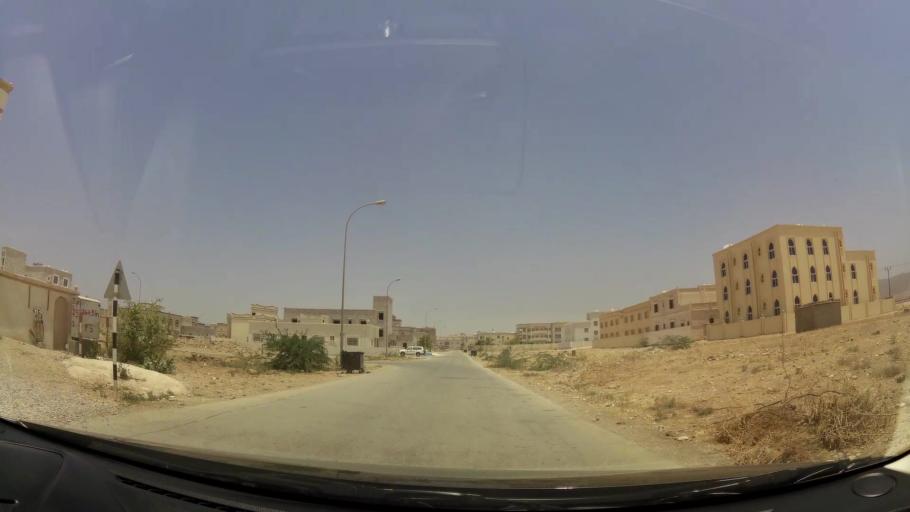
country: OM
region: Zufar
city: Salalah
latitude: 17.0982
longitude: 54.1577
